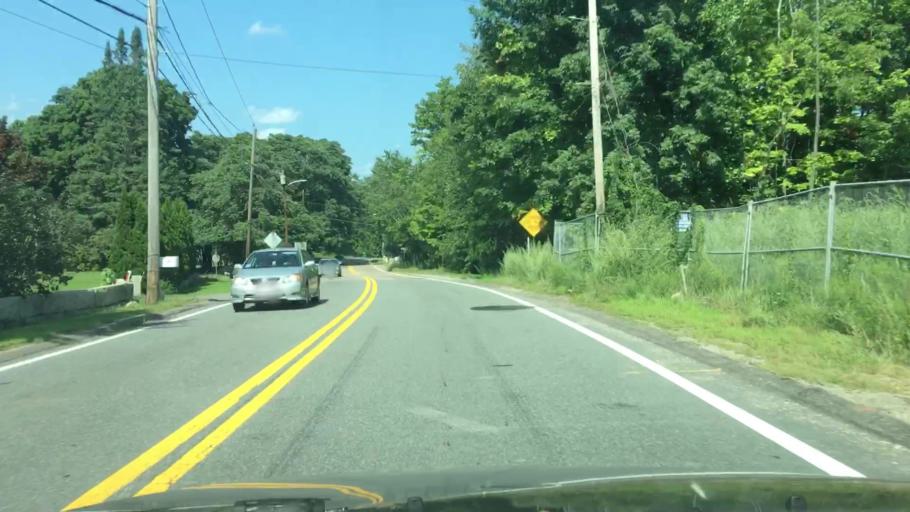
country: US
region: Massachusetts
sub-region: Worcester County
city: Milford
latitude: 42.1646
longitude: -71.4805
